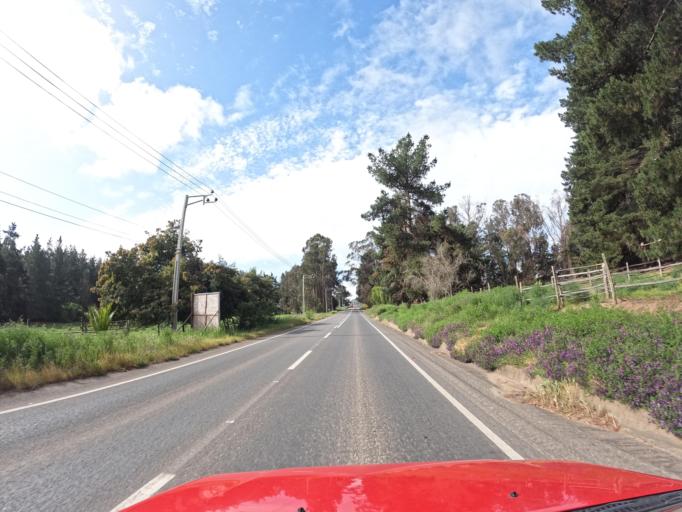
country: CL
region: O'Higgins
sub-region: Provincia de Colchagua
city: Santa Cruz
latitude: -34.3704
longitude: -71.9661
